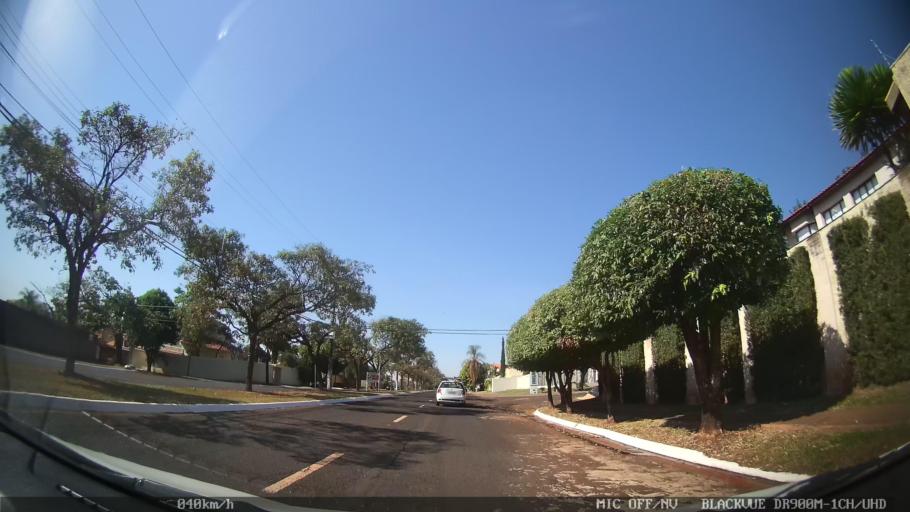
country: BR
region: Sao Paulo
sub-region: Ribeirao Preto
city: Ribeirao Preto
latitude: -21.2132
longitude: -47.7845
